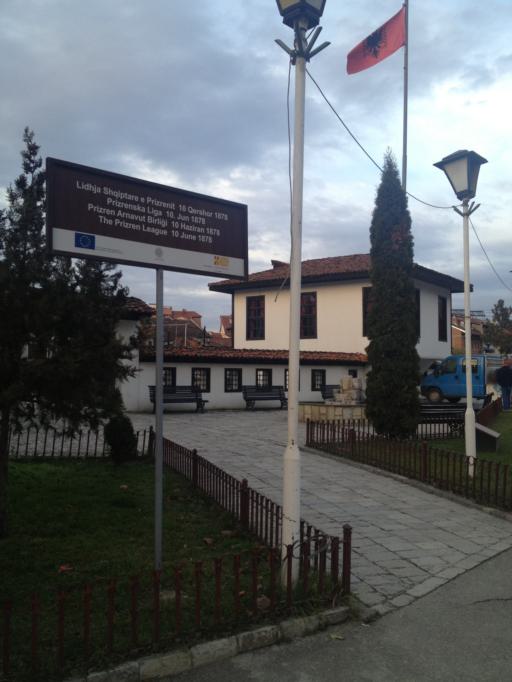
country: XK
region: Prizren
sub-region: Prizren
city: Prizren
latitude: 42.2112
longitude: 20.7438
